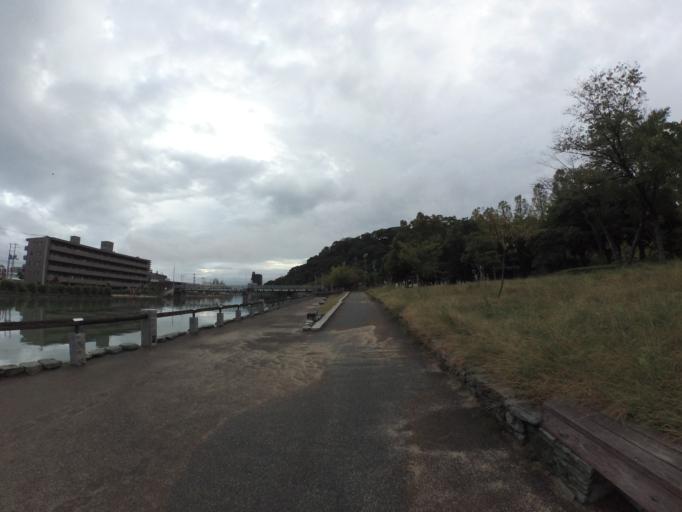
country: JP
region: Tokushima
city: Tokushima-shi
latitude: 34.0771
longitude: 134.5522
